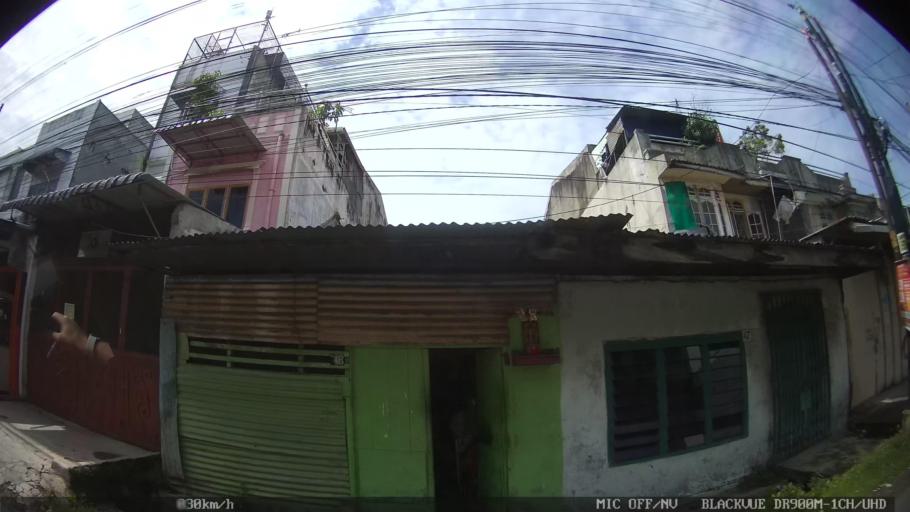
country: ID
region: North Sumatra
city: Medan
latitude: 3.5874
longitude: 98.7101
